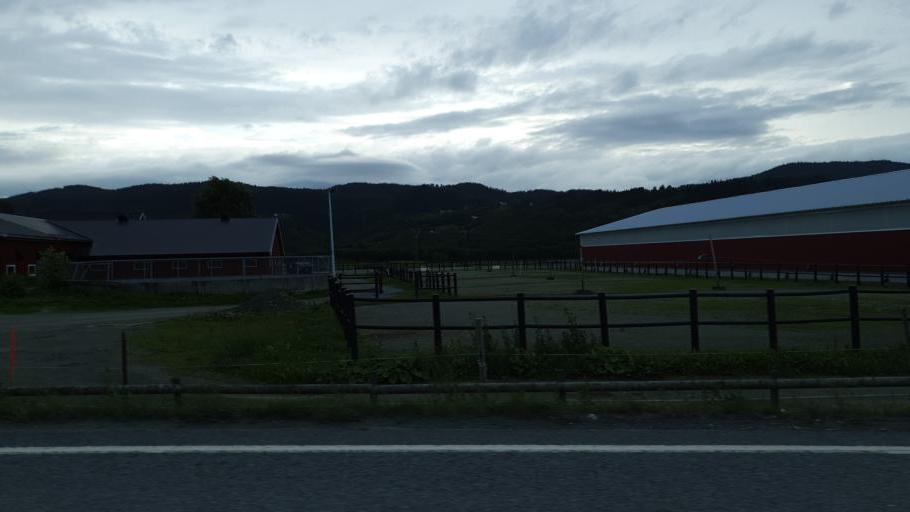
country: NO
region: Sor-Trondelag
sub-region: Melhus
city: Melhus
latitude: 63.2374
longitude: 10.2769
